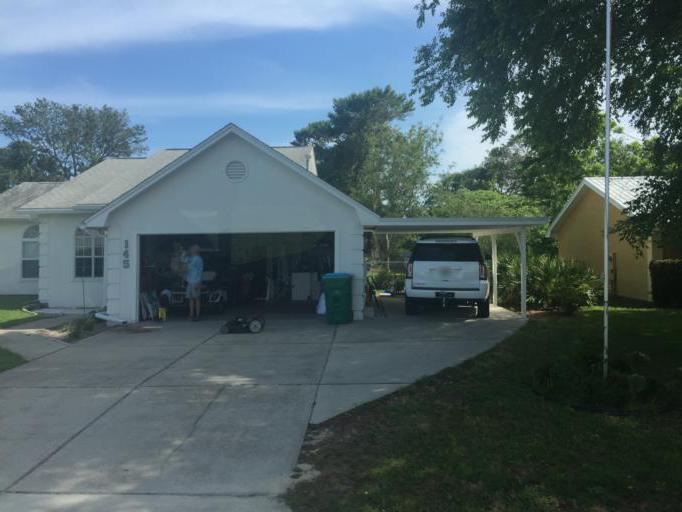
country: US
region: Florida
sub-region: Bay County
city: Laguna Beach
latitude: 30.2608
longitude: -85.9640
